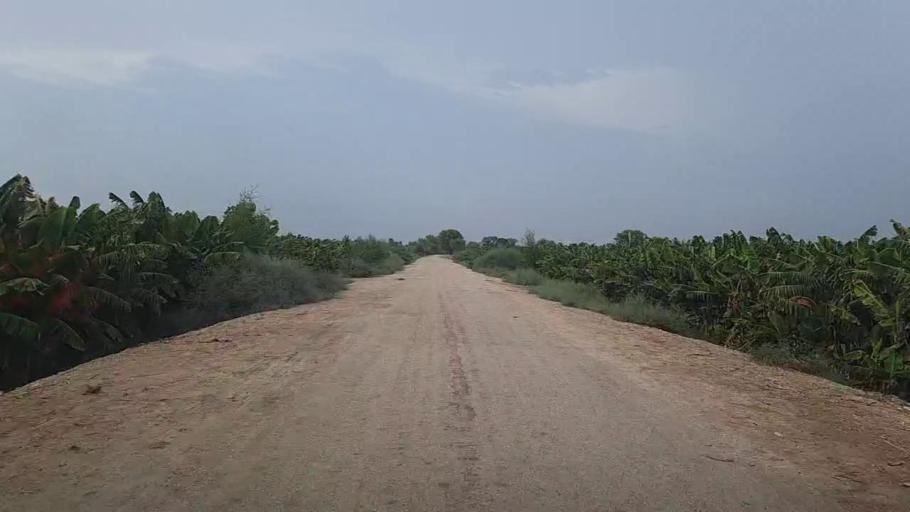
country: PK
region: Sindh
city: Karaundi
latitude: 26.9801
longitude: 68.4339
